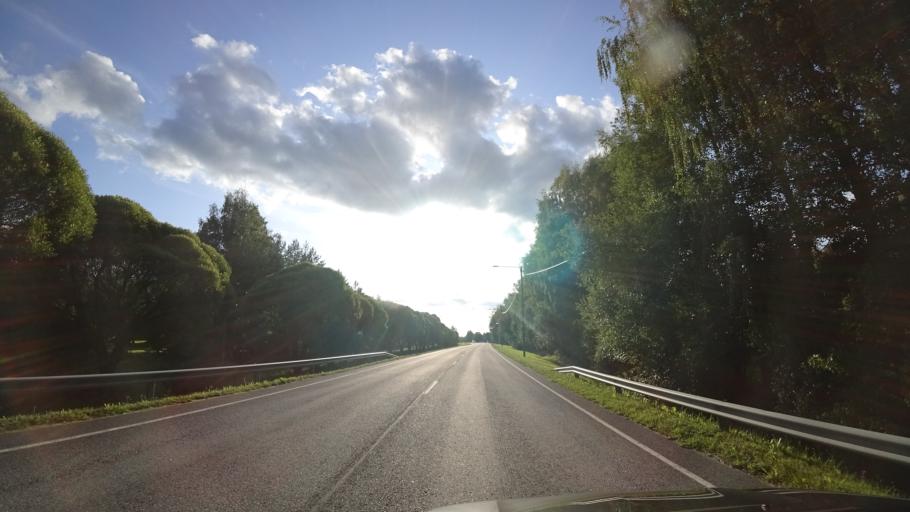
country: FI
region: Haeme
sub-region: Haemeenlinna
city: Lammi
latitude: 61.0776
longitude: 25.0184
